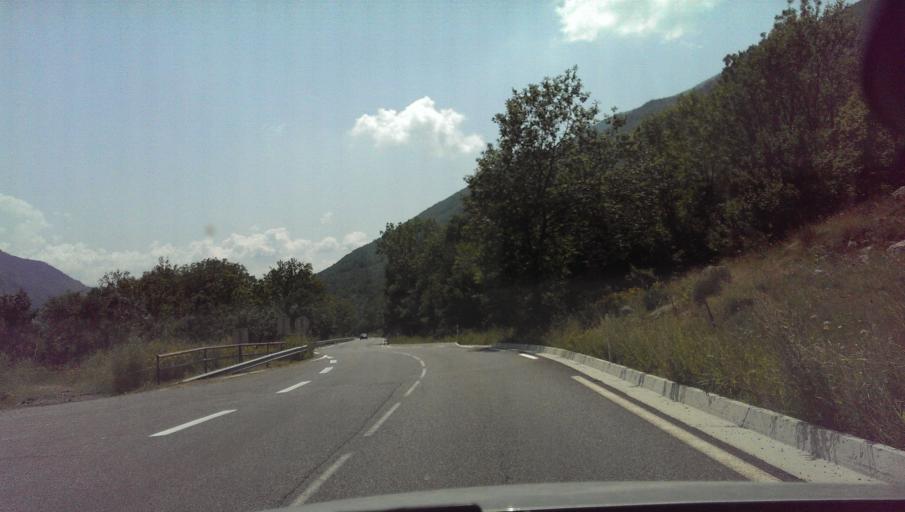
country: ES
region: Catalonia
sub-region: Provincia de Girona
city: Guils de Cerdanya
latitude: 42.5025
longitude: 1.8360
